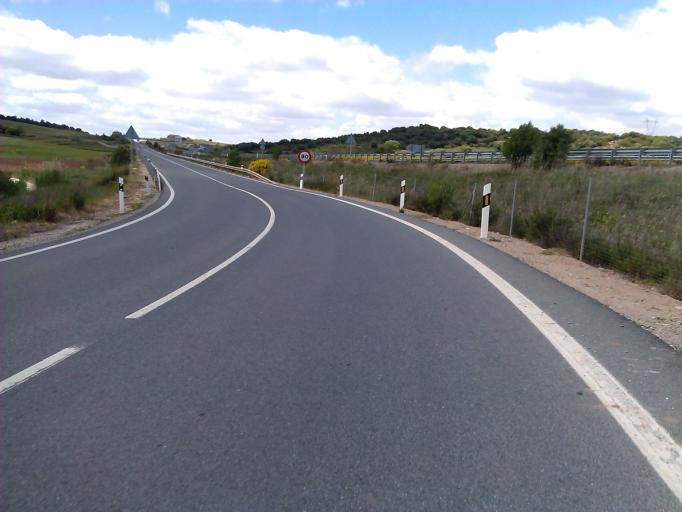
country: ES
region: La Rioja
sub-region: Provincia de La Rioja
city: Ventosa
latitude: 42.4131
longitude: -2.6294
